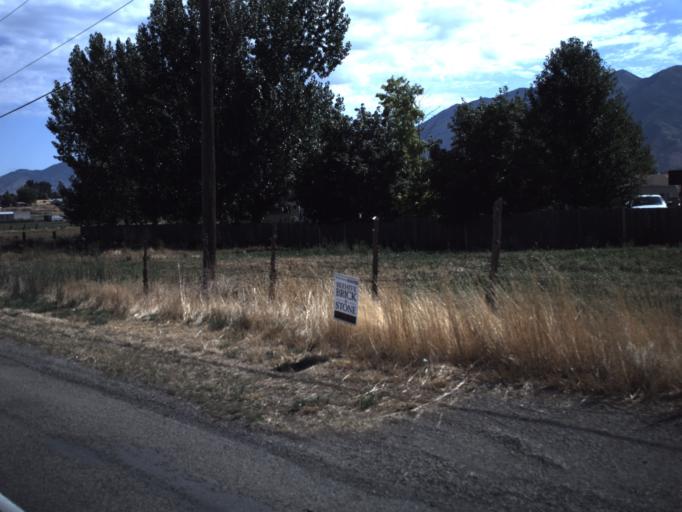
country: US
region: Utah
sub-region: Utah County
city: Salem
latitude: 40.0636
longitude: -111.6671
